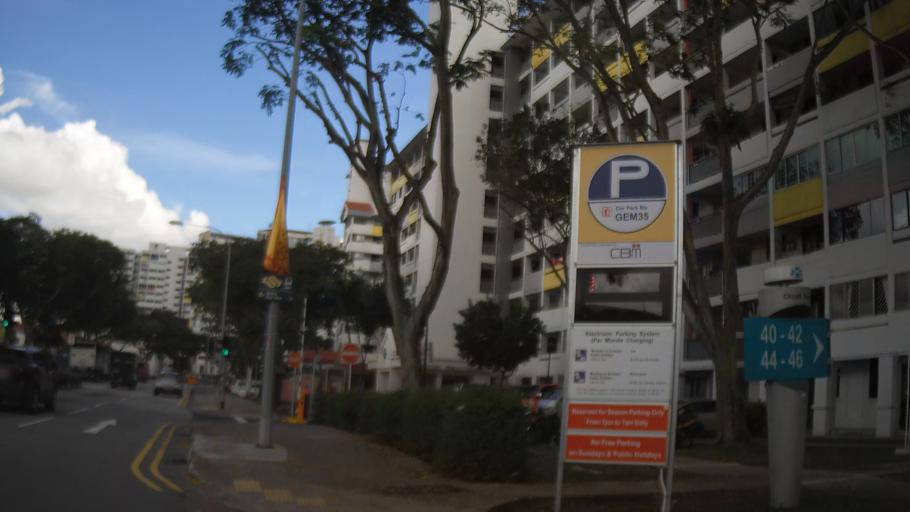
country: SG
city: Singapore
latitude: 1.3270
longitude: 103.8854
